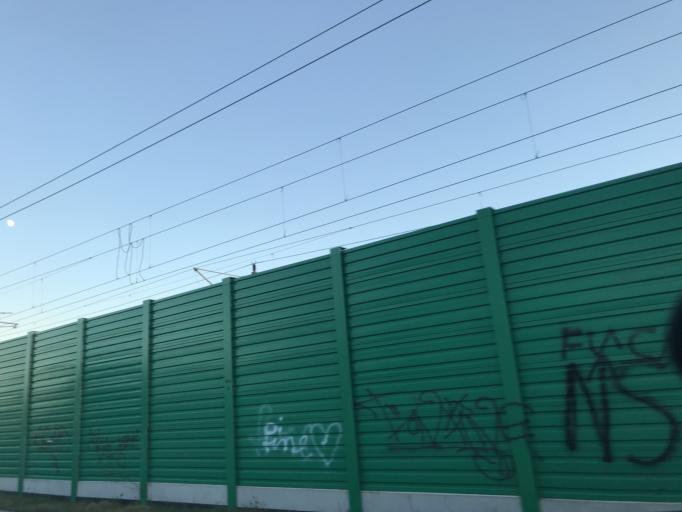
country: DE
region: Brandenburg
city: Rathenow
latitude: 52.5957
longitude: 12.3351
